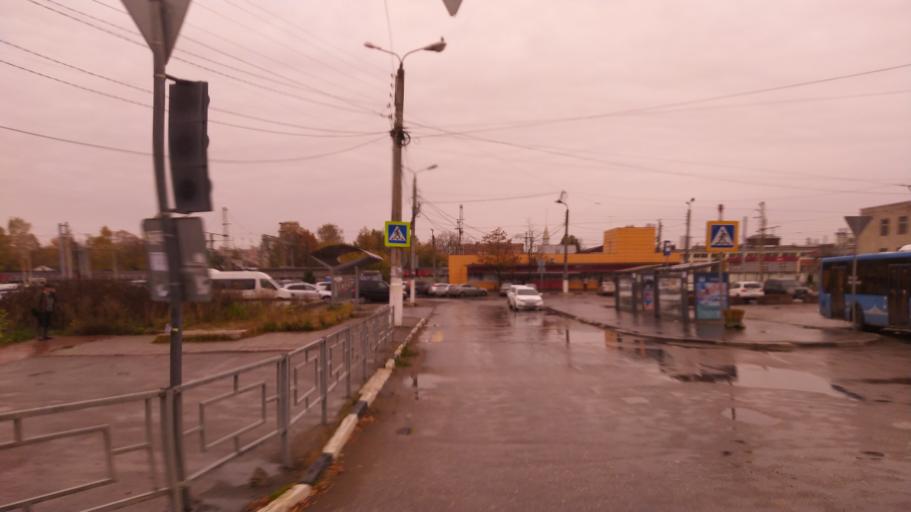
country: RU
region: Tverskaya
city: Tver
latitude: 56.8361
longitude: 35.8952
